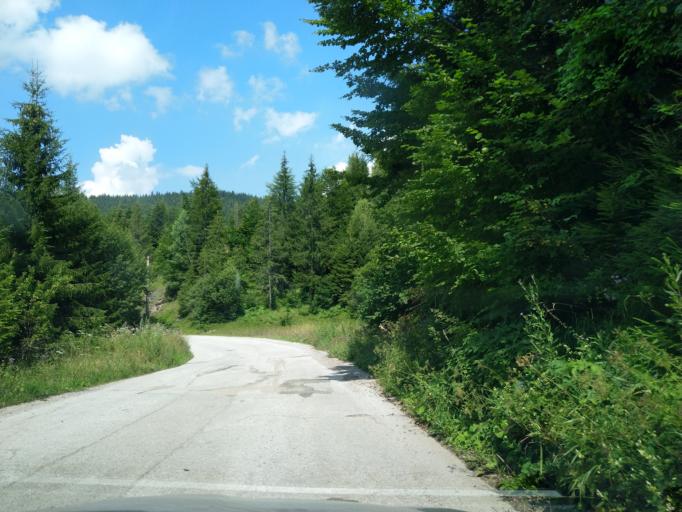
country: RS
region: Central Serbia
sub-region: Zlatiborski Okrug
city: Nova Varos
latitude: 43.5443
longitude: 19.9020
